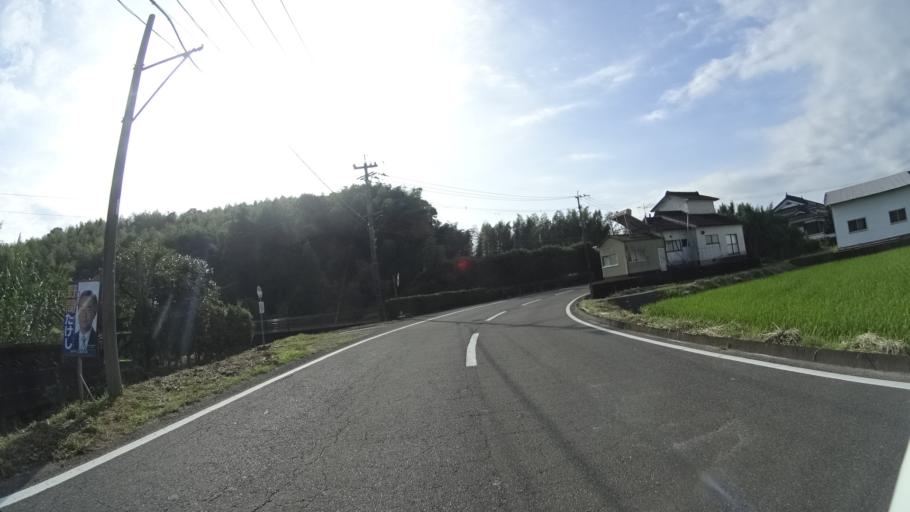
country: JP
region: Kagoshima
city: Okuchi-shinohara
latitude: 32.0259
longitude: 130.6039
